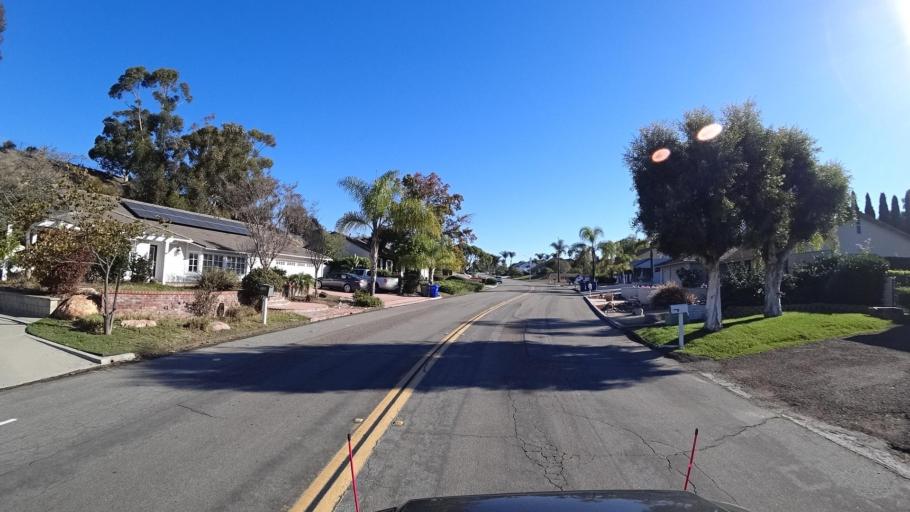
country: US
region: California
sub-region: San Diego County
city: Bonita
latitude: 32.6839
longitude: -117.0250
